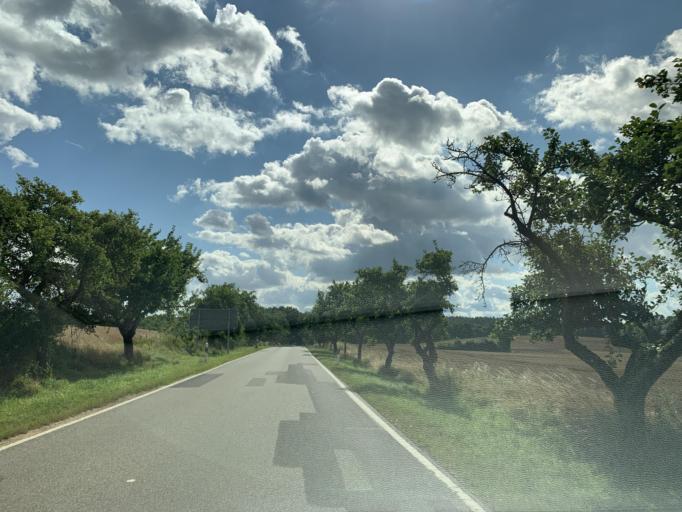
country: DE
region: Mecklenburg-Vorpommern
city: Neustrelitz
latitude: 53.4048
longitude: 13.1191
